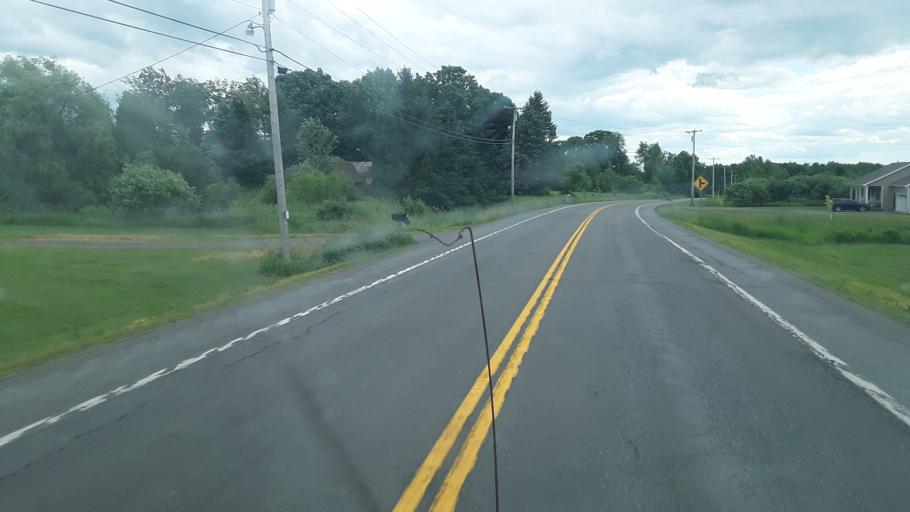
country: US
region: New York
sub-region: Oneida County
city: Rome
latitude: 43.3302
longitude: -75.4769
